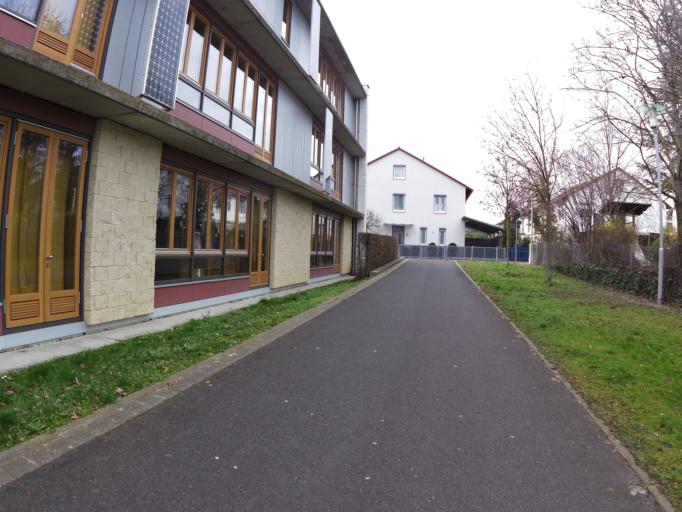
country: DE
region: Bavaria
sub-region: Regierungsbezirk Unterfranken
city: Kitzingen
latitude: 49.7282
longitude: 10.1629
